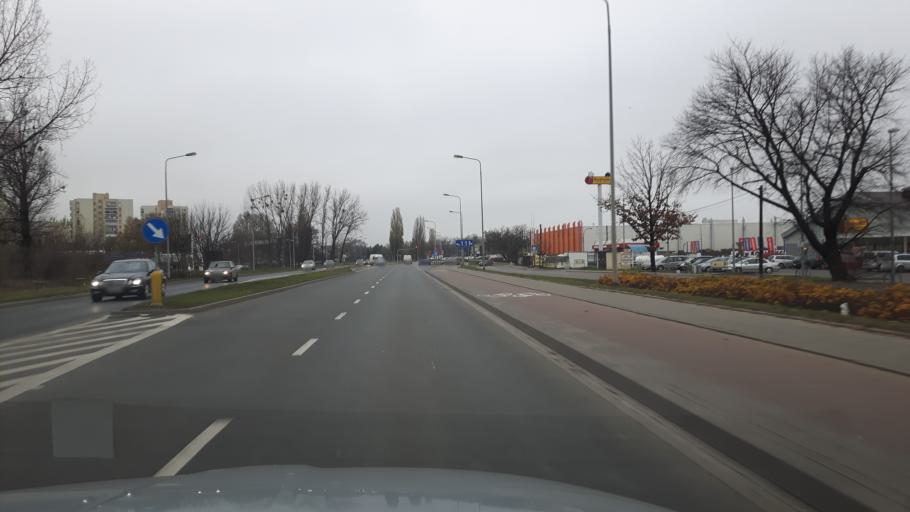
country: PL
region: Masovian Voivodeship
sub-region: Warszawa
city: Targowek
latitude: 52.2729
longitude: 21.0685
